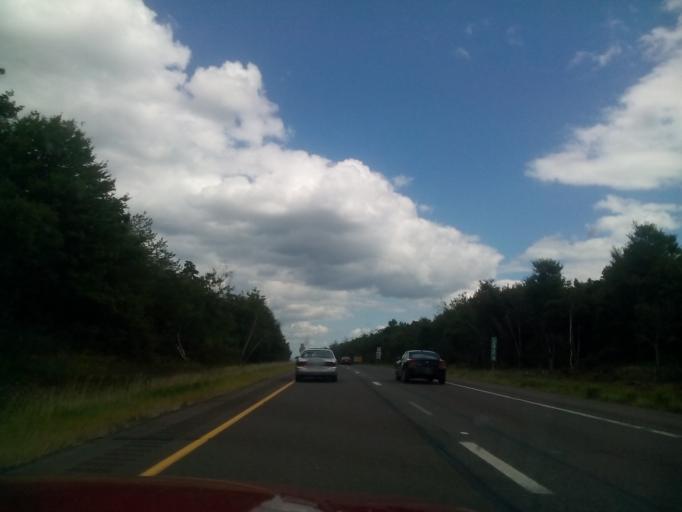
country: US
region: Pennsylvania
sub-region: Monroe County
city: Emerald Lakes
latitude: 41.0702
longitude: -75.4088
